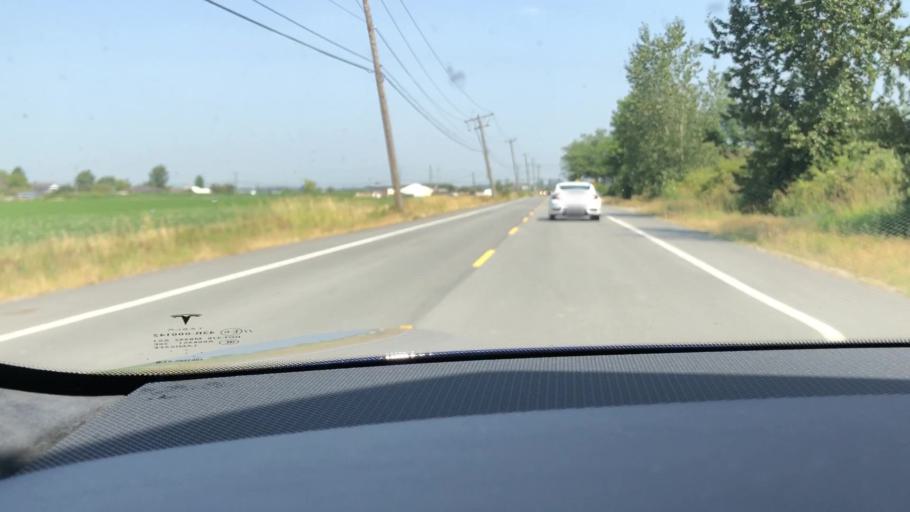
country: CA
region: British Columbia
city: Ladner
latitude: 49.0511
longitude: -123.0798
